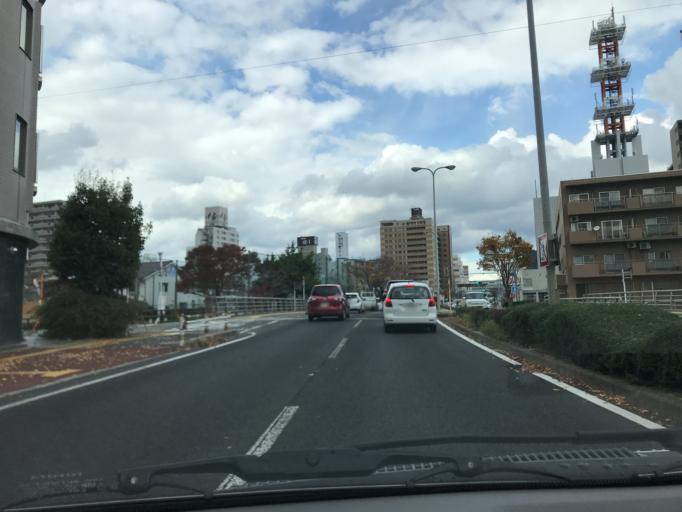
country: JP
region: Shimane
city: Matsue-shi
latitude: 35.4608
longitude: 133.0656
